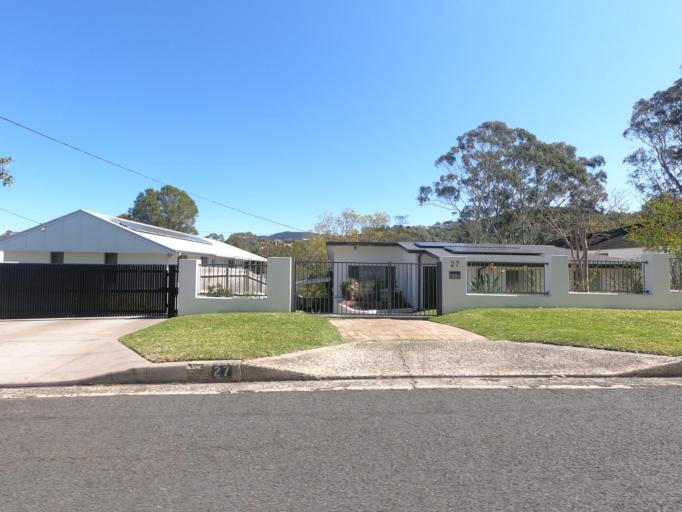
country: AU
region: New South Wales
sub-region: Wollongong
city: Mount Keira
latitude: -34.4265
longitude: 150.8507
